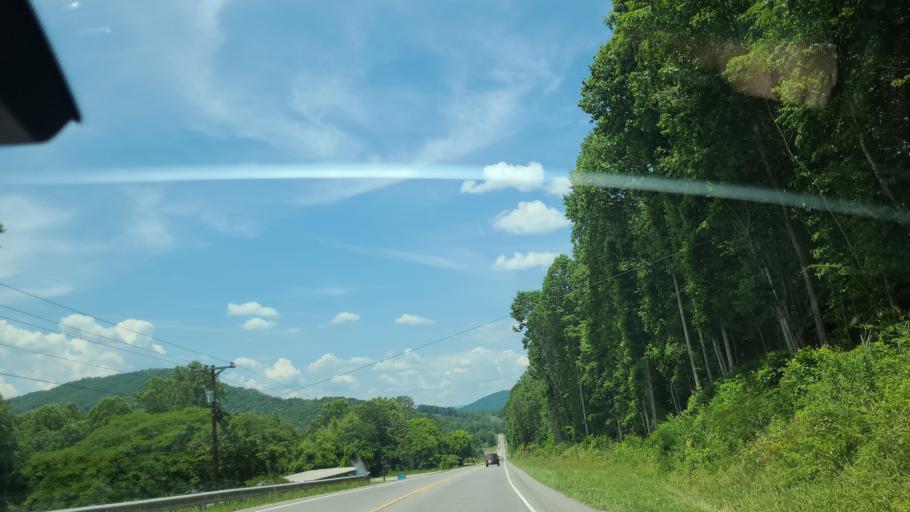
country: US
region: North Carolina
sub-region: Clay County
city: Hayesville
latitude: 35.0339
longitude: -83.8672
